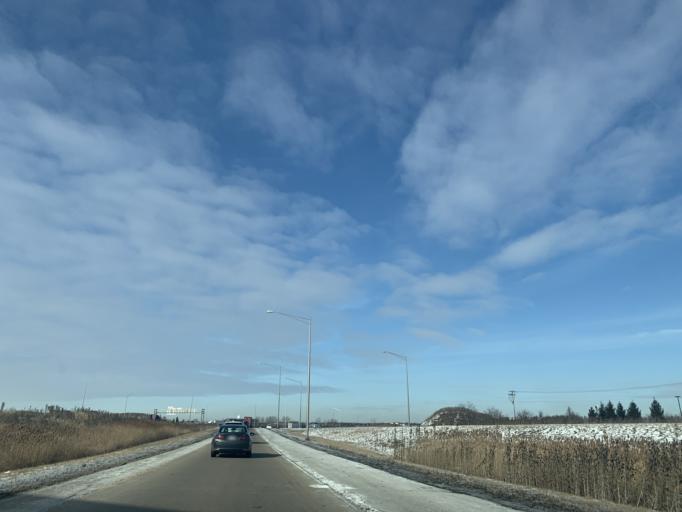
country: US
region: Illinois
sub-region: Will County
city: Bolingbrook
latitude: 41.7076
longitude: -88.0294
